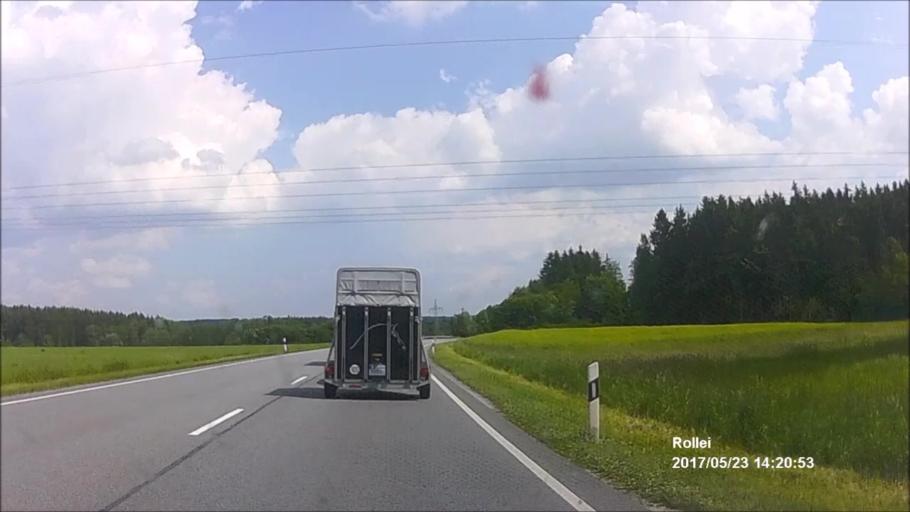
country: DE
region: Bavaria
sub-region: Upper Bavaria
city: Babensham
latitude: 48.0643
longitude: 12.2527
